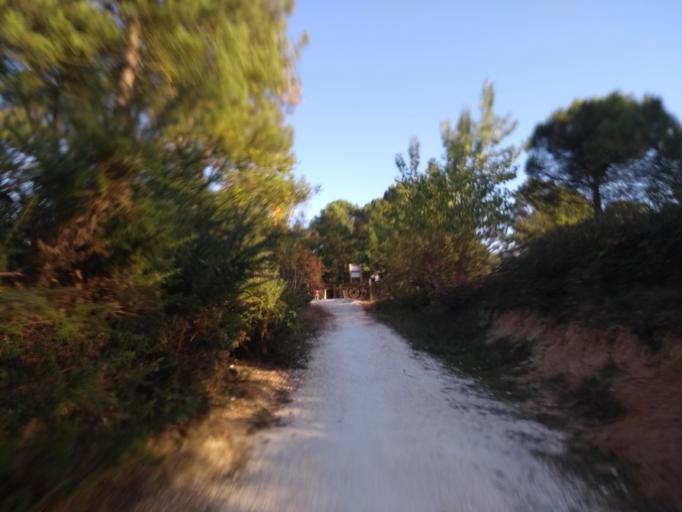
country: FR
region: Aquitaine
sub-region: Departement de la Gironde
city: Pessac
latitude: 44.8038
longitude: -0.6879
